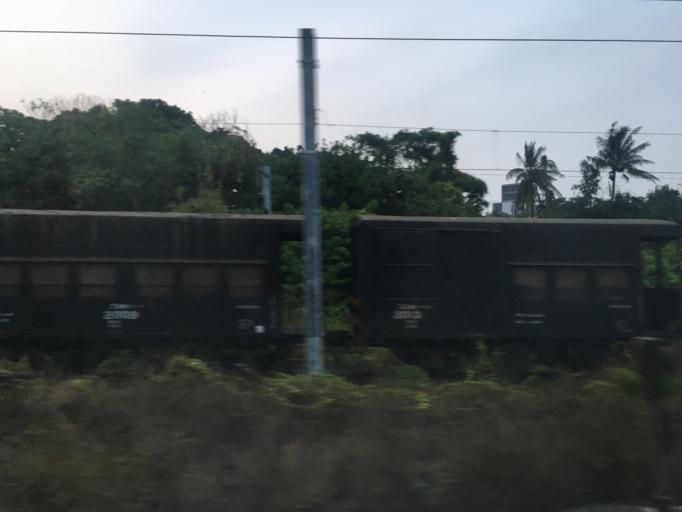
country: TW
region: Taiwan
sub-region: Pingtung
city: Pingtung
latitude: 22.6601
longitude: 120.4222
